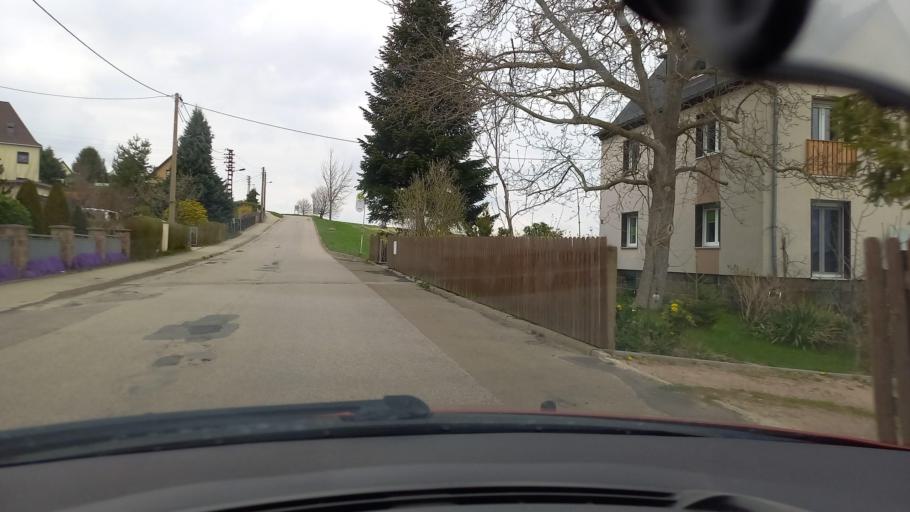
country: DE
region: Saxony
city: Wilkau-Hasslau
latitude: 50.6697
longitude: 12.4992
